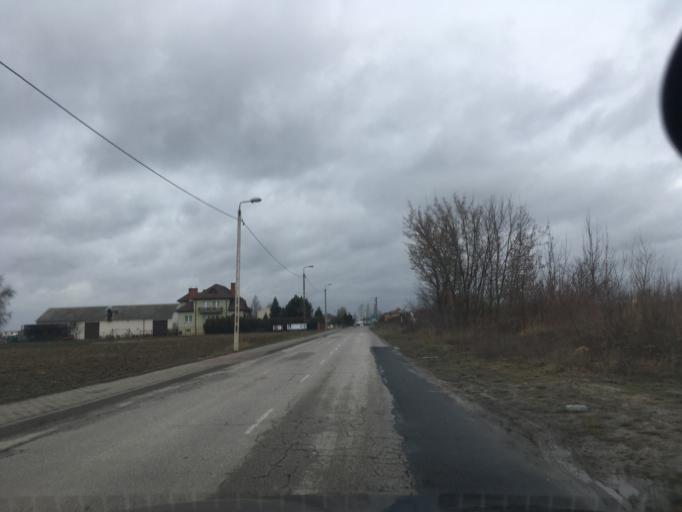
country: PL
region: Masovian Voivodeship
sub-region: Powiat piaseczynski
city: Lesznowola
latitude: 52.1182
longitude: 20.9304
